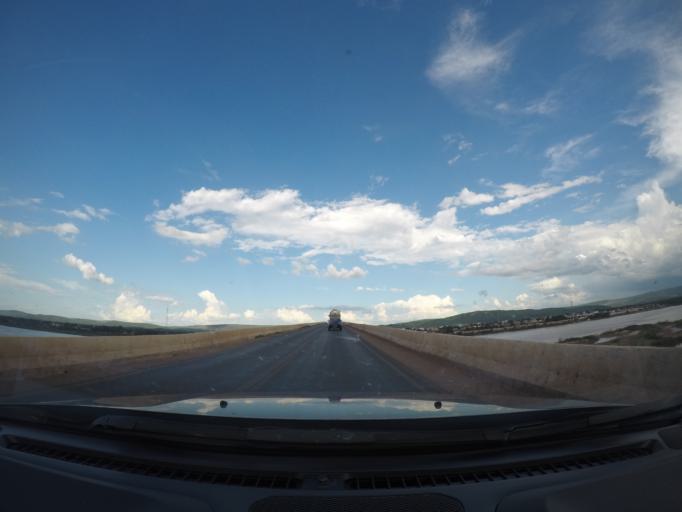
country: BR
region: Bahia
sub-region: Ibotirama
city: Ibotirama
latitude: -12.1813
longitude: -43.2295
